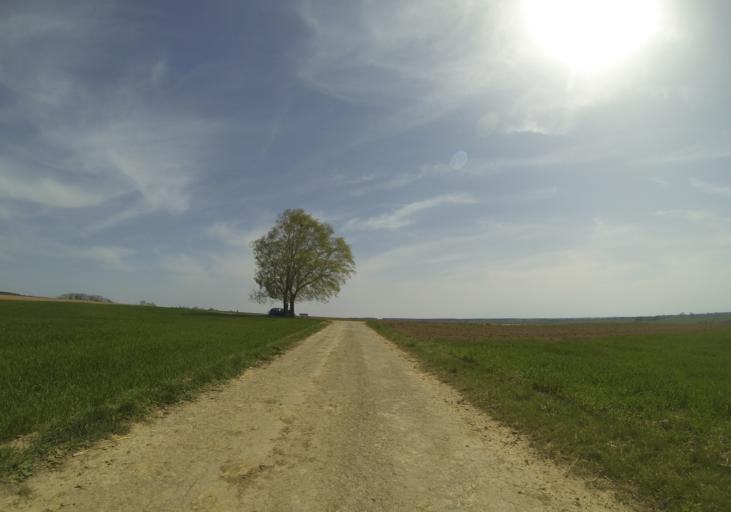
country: DE
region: Baden-Wuerttemberg
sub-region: Tuebingen Region
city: Burgrieden
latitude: 48.2509
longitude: 9.9263
